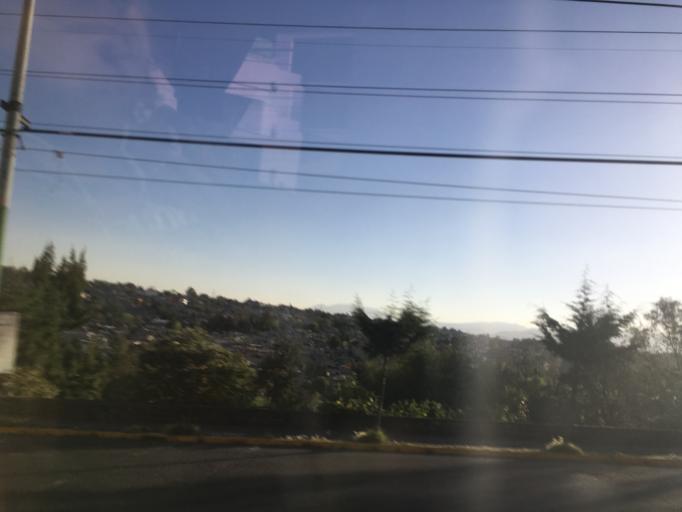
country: MX
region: Mexico City
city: Polanco
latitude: 19.3975
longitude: -99.2115
